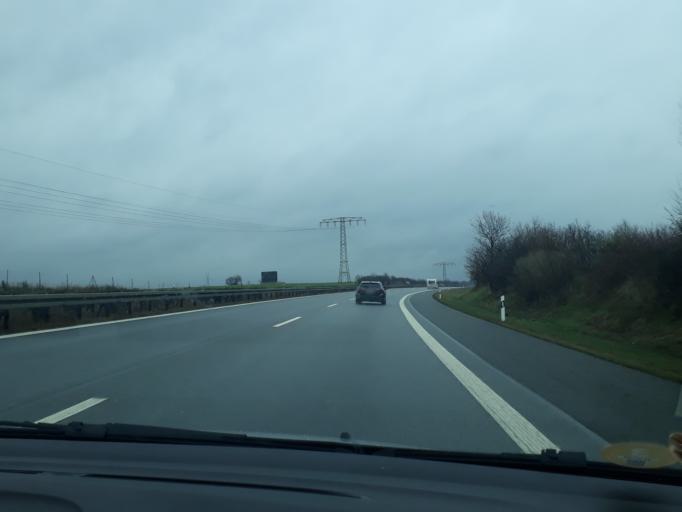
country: DE
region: Saxony
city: Bautzen
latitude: 51.1982
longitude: 14.4309
